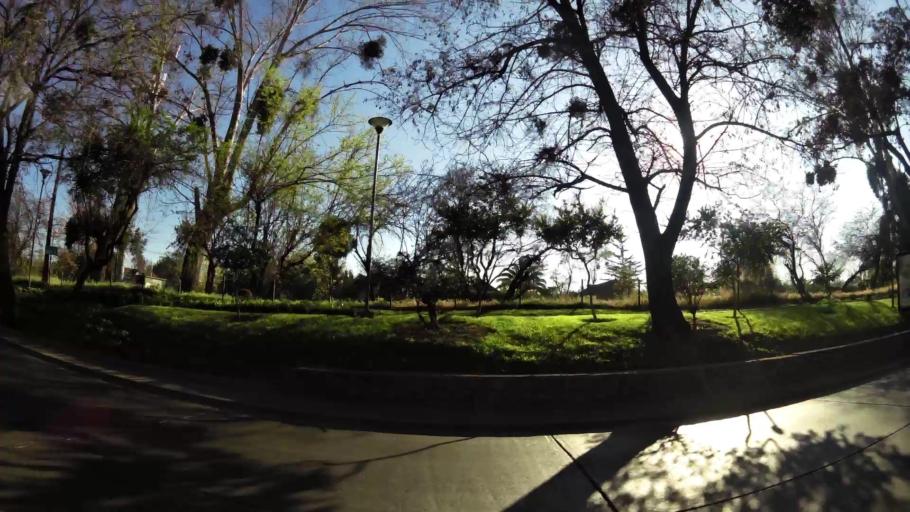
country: CL
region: Santiago Metropolitan
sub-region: Provincia de Santiago
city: Villa Presidente Frei, Nunoa, Santiago, Chile
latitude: -33.4477
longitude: -70.5636
